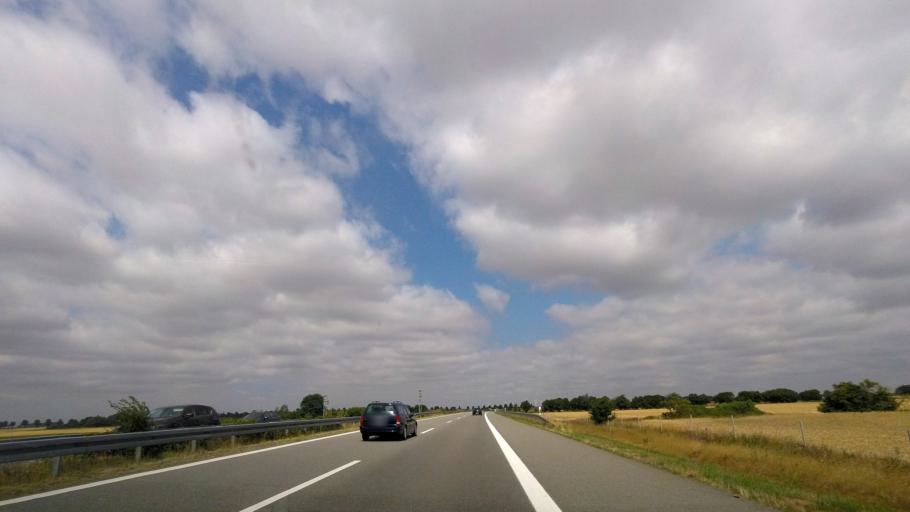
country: DE
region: Mecklenburg-Vorpommern
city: Gormin
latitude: 54.0058
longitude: 13.3015
